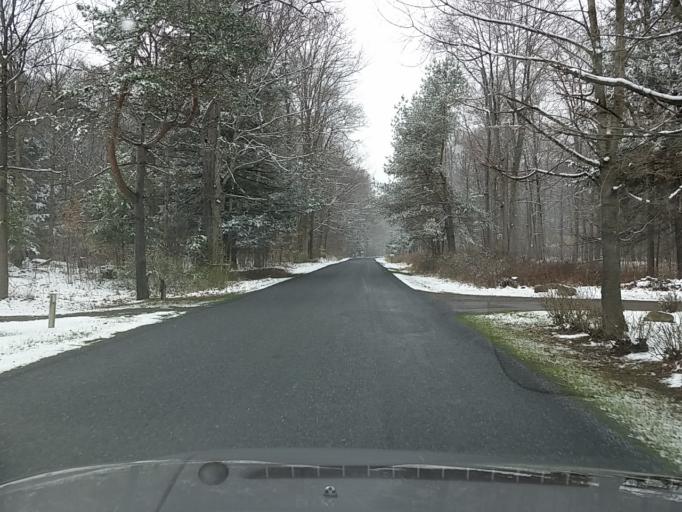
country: US
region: Pennsylvania
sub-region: Sullivan County
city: Laporte
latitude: 41.3056
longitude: -76.4195
